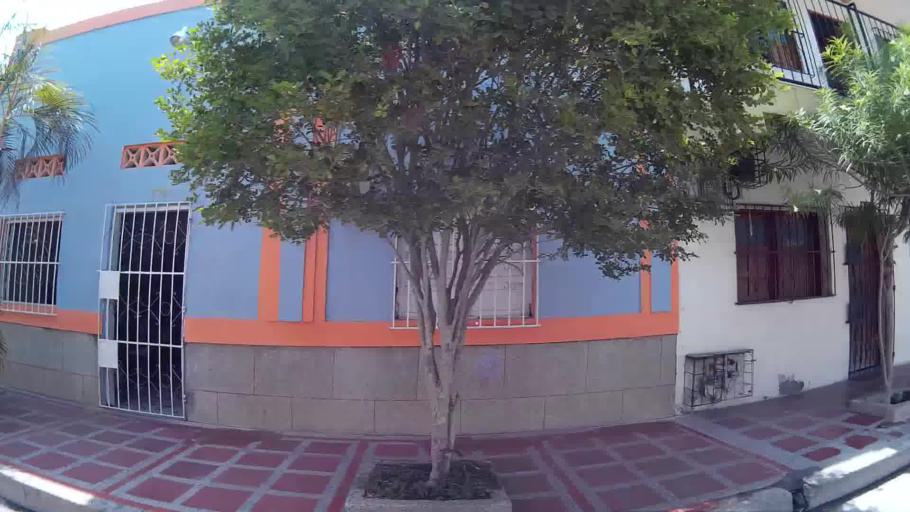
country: CO
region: Magdalena
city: Cienaga
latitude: 11.0141
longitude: -74.2473
